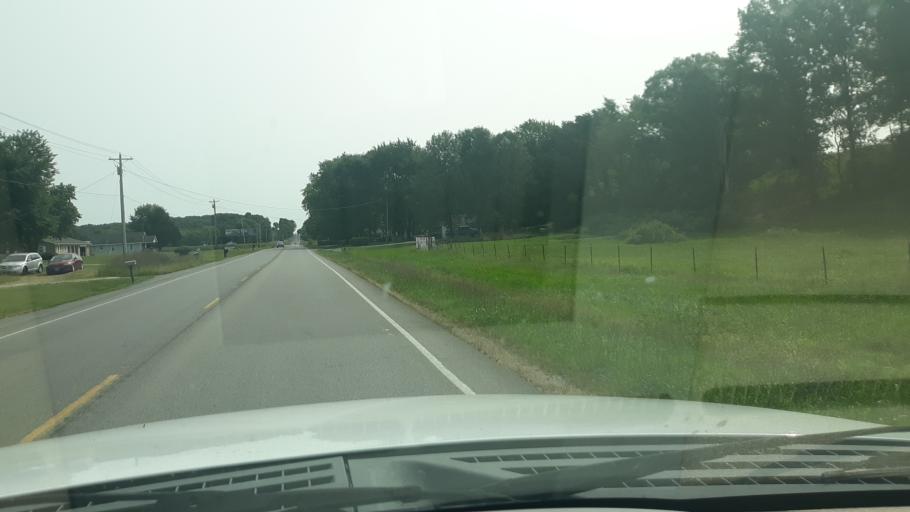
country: US
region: Indiana
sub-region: Gibson County
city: Owensville
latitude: 38.3559
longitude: -87.6713
